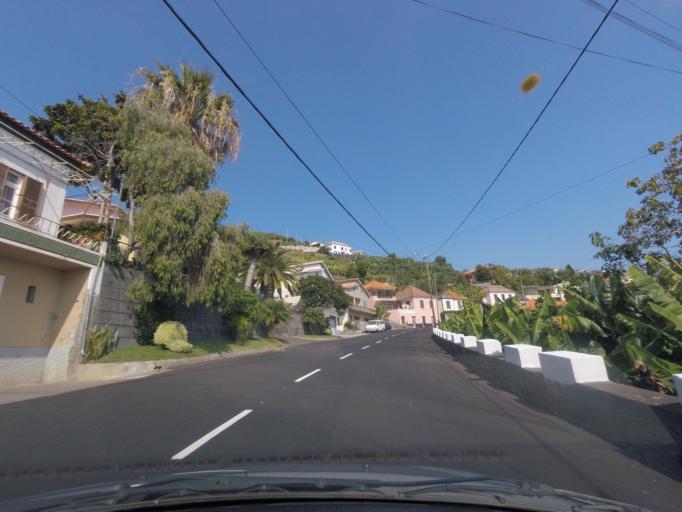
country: PT
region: Madeira
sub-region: Ribeira Brava
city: Campanario
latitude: 32.6698
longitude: -17.0562
